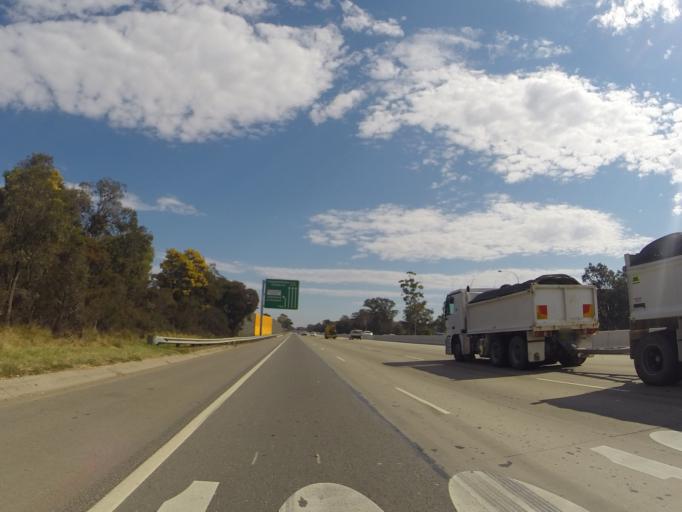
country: AU
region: New South Wales
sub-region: Bankstown
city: Milperra
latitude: -33.9418
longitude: 150.9399
